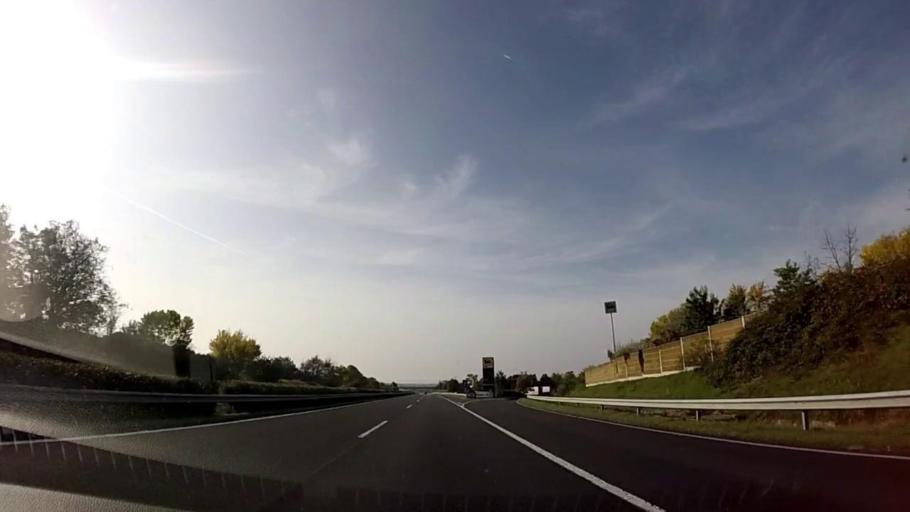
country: HU
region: Somogy
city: Balatonszabadi
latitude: 46.9575
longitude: 18.1559
